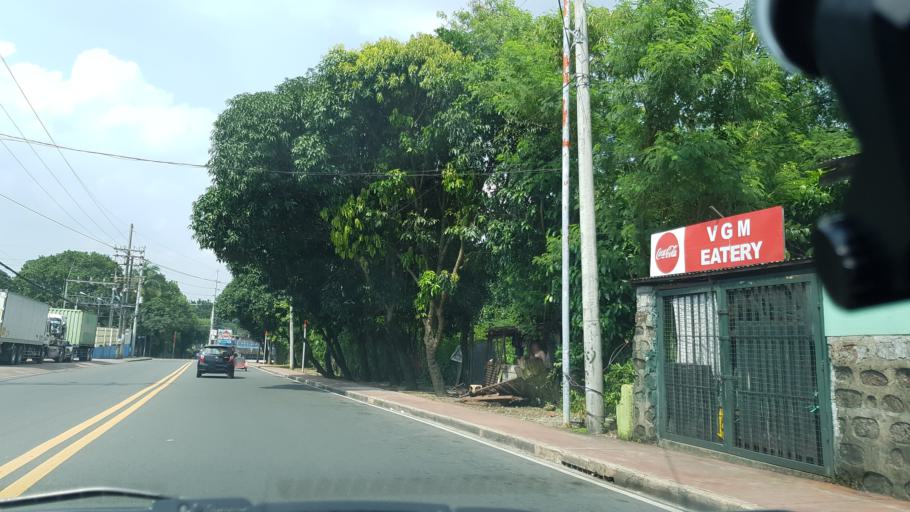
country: PH
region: Calabarzon
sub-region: Province of Rizal
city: Antipolo
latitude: 14.6619
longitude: 121.1186
